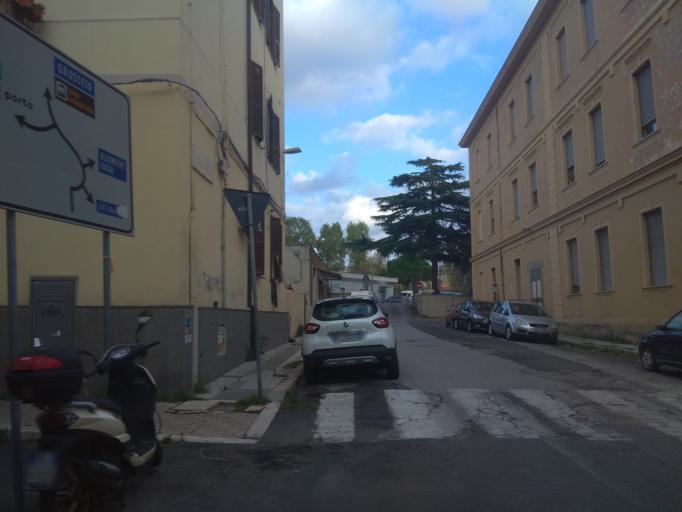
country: IT
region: Latium
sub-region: Citta metropolitana di Roma Capitale
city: Civitavecchia
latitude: 42.0962
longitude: 11.7897
